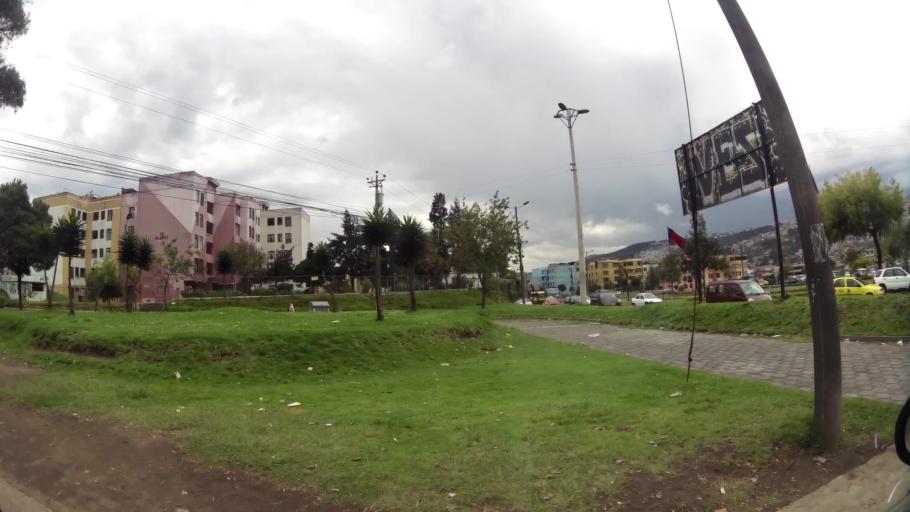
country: EC
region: Pichincha
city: Quito
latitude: -0.2828
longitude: -78.5443
